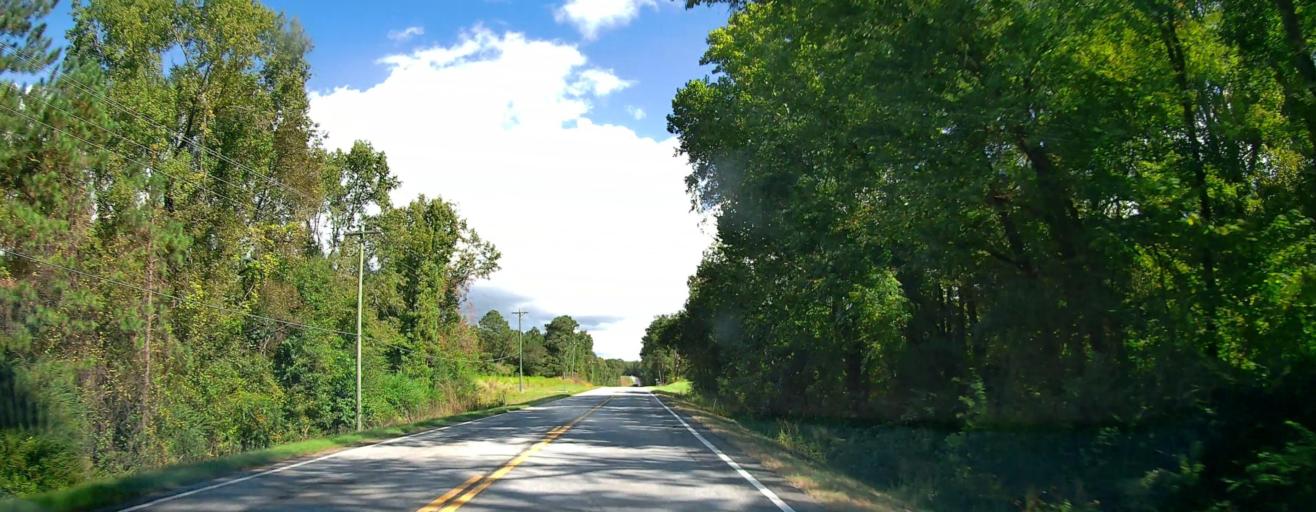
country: US
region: Georgia
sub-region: Jones County
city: Gray
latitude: 32.9445
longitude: -83.4754
